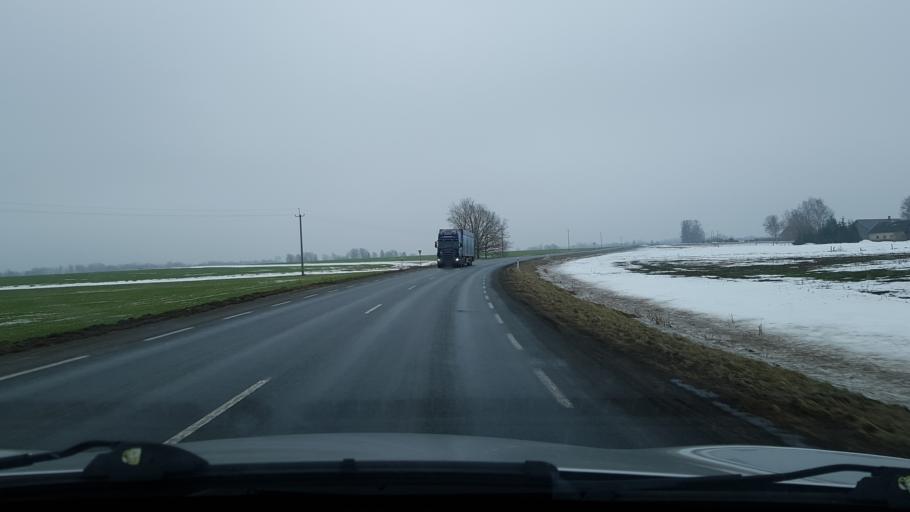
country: EE
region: Viljandimaa
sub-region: Viiratsi vald
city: Viiratsi
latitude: 58.2502
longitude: 25.8406
